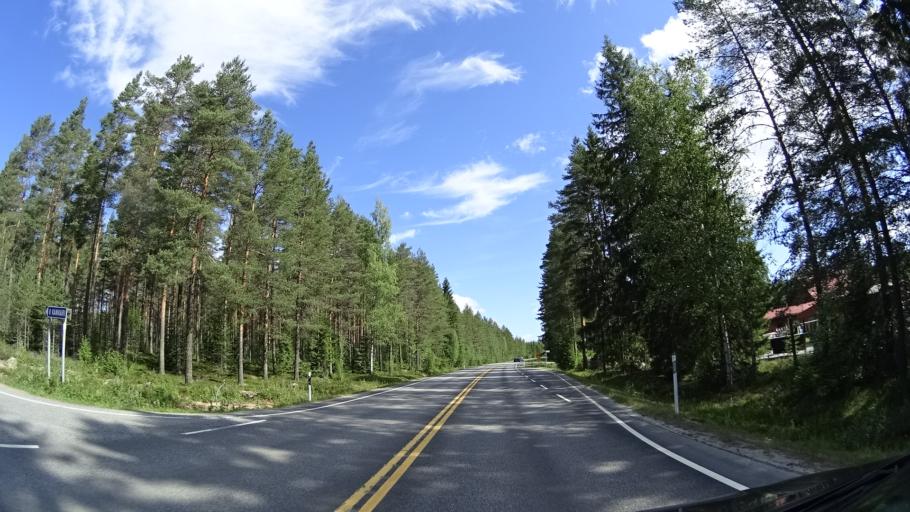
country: FI
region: Pirkanmaa
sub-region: Luoteis-Pirkanmaa
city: Kihnioe
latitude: 62.1227
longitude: 23.1095
